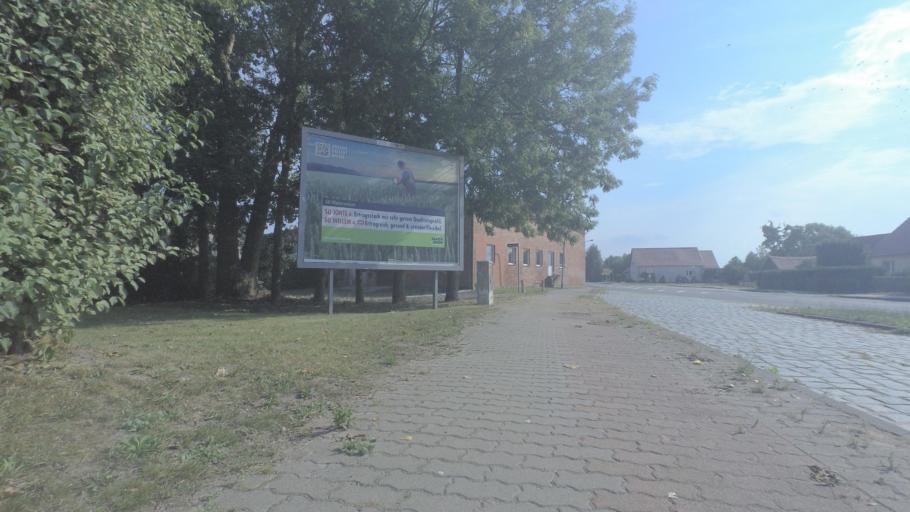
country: DE
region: Mecklenburg-Vorpommern
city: Grimmen
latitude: 54.0555
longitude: 13.1191
